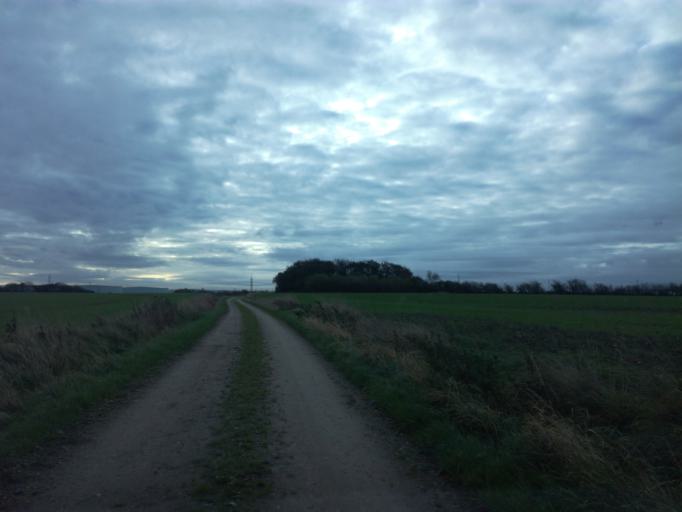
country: DK
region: South Denmark
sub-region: Fredericia Kommune
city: Fredericia
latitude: 55.6054
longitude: 9.7442
